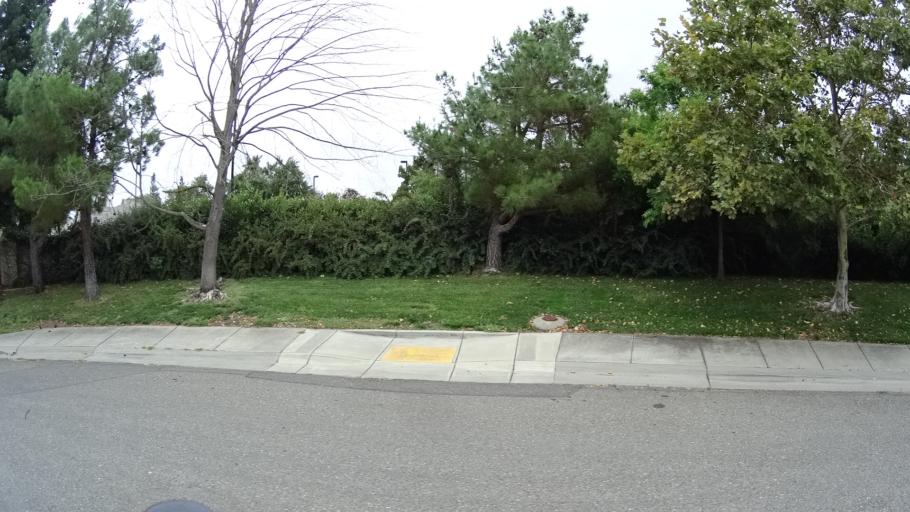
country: US
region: California
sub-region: Sacramento County
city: Laguna
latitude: 38.4211
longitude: -121.4505
